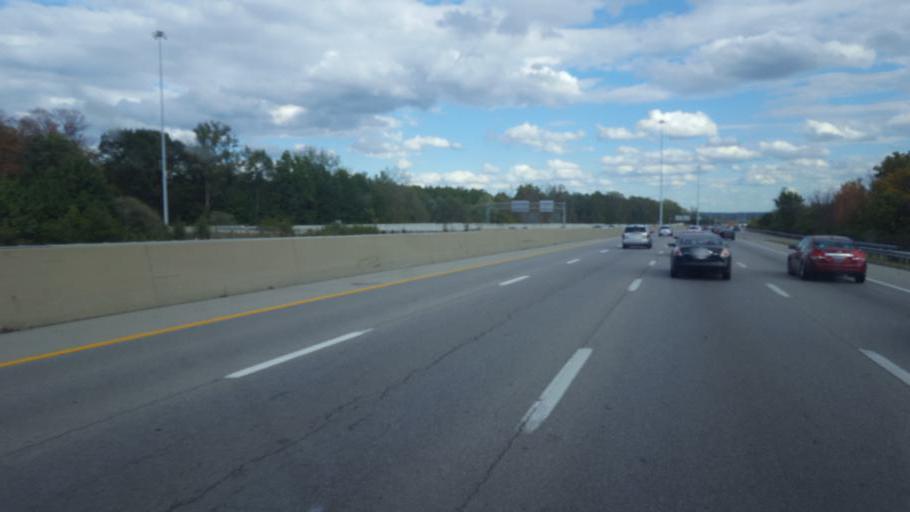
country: US
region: Ohio
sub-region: Franklin County
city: Minerva Park
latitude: 40.1101
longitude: -82.9742
